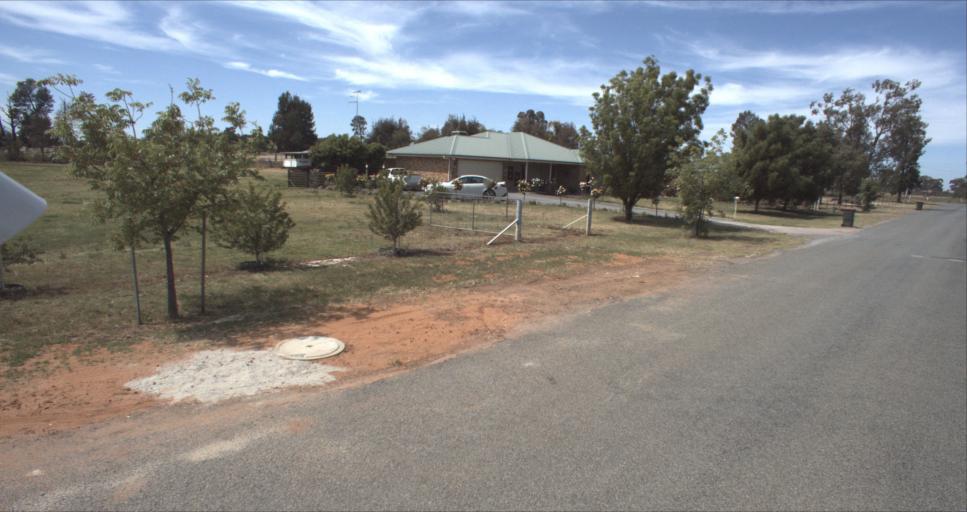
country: AU
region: New South Wales
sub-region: Leeton
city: Leeton
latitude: -34.5625
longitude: 146.4185
